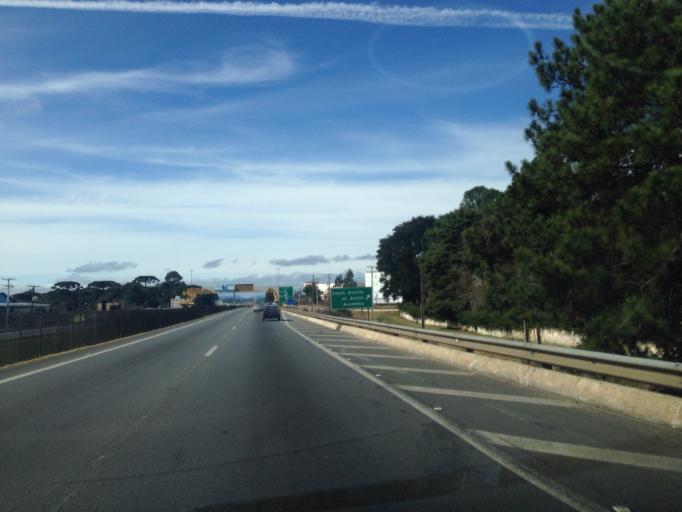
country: BR
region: Parana
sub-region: Sao Jose Dos Pinhais
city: Sao Jose dos Pinhais
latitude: -25.5074
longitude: -49.1376
